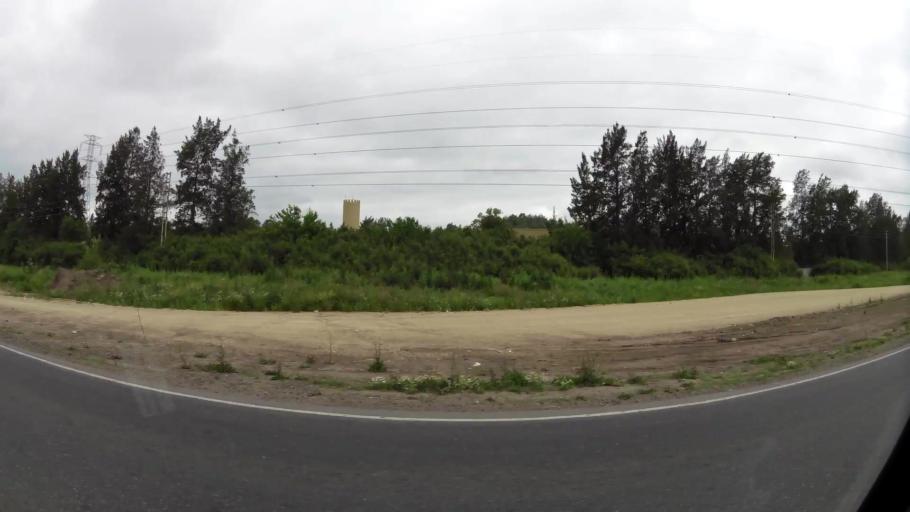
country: AR
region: Buenos Aires
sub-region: Partido de Ezeiza
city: Ezeiza
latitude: -34.9012
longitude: -58.5091
